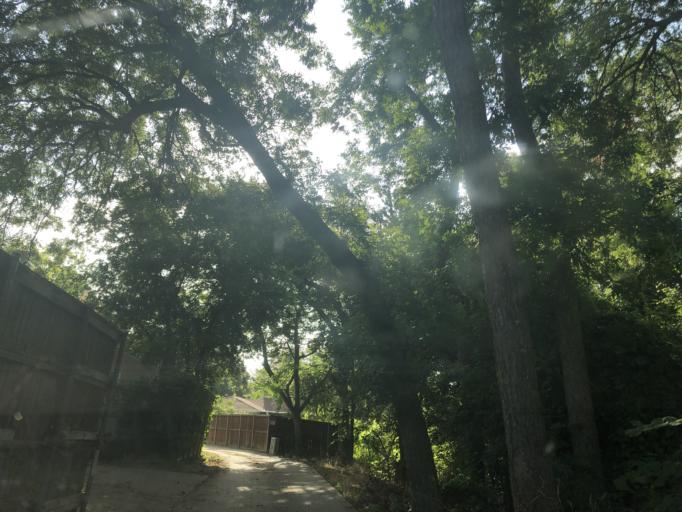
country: US
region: Texas
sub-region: Dallas County
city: Garland
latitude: 32.8551
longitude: -96.6235
